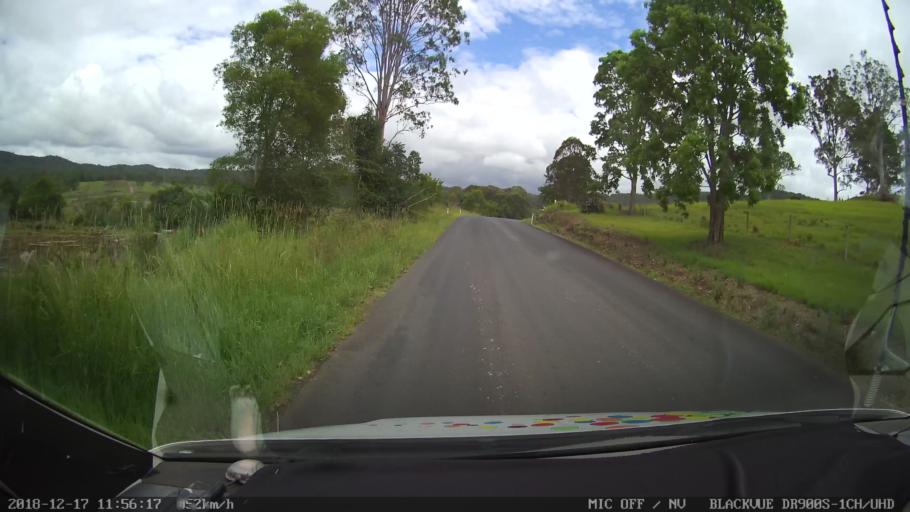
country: AU
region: New South Wales
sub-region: Kyogle
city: Kyogle
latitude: -28.5488
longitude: 152.5813
